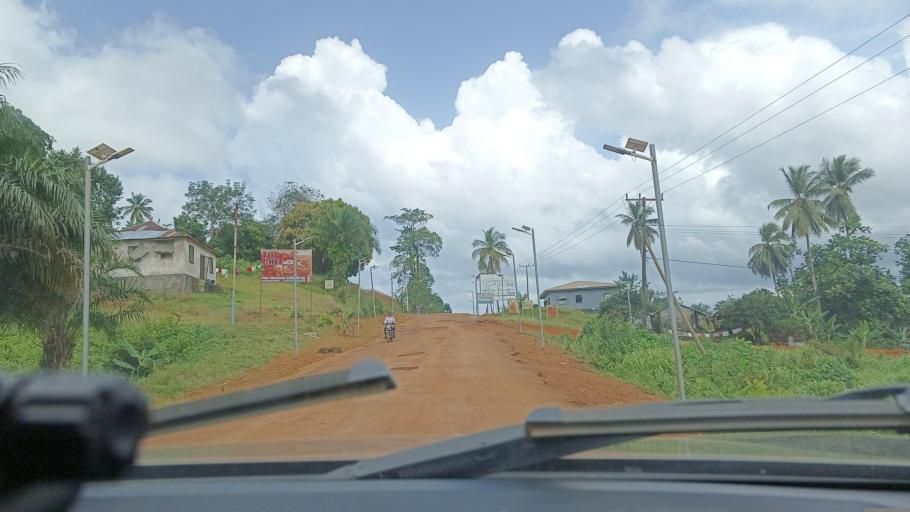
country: LR
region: Grand Cape Mount
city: Robertsport
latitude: 6.7519
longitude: -11.3627
